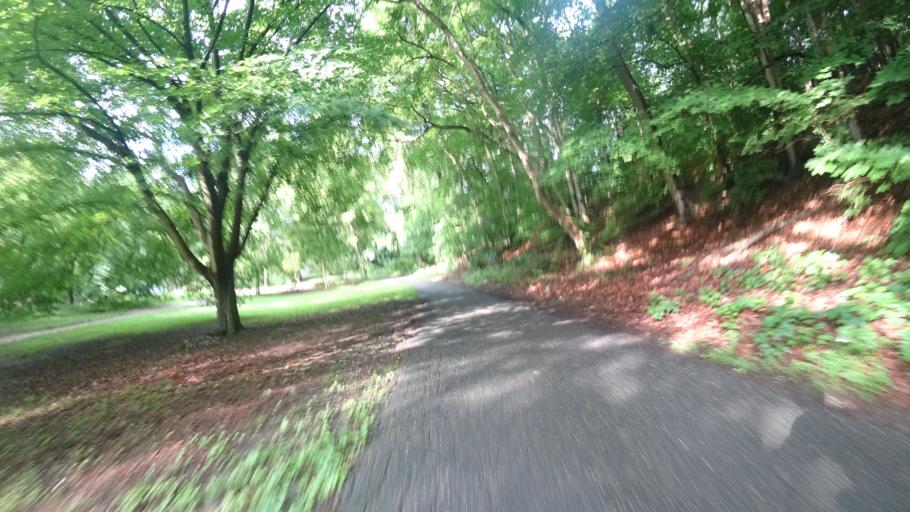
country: US
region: Maryland
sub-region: Montgomery County
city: Chevy Chase
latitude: 38.9420
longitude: -77.0516
